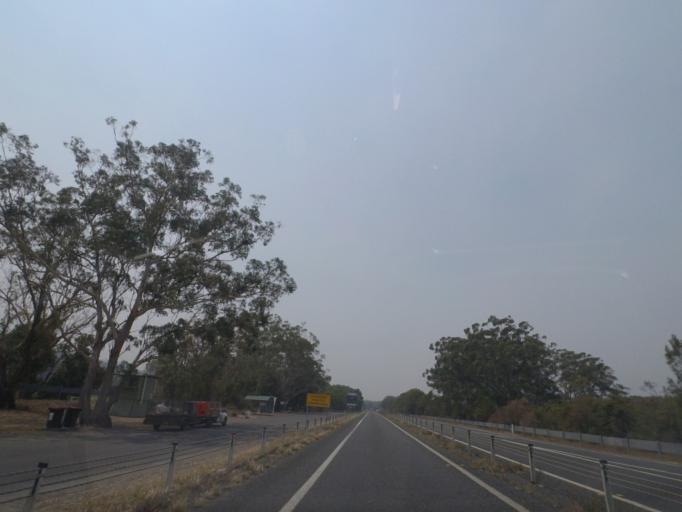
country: AU
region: New South Wales
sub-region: Ballina
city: Ballina
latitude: -28.9345
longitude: 153.4722
